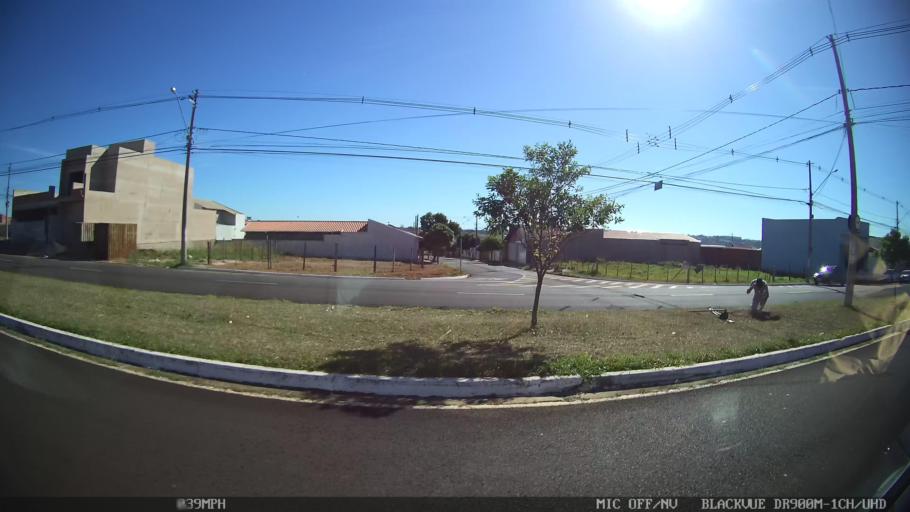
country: BR
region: Sao Paulo
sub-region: Franca
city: Franca
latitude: -20.5643
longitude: -47.3510
